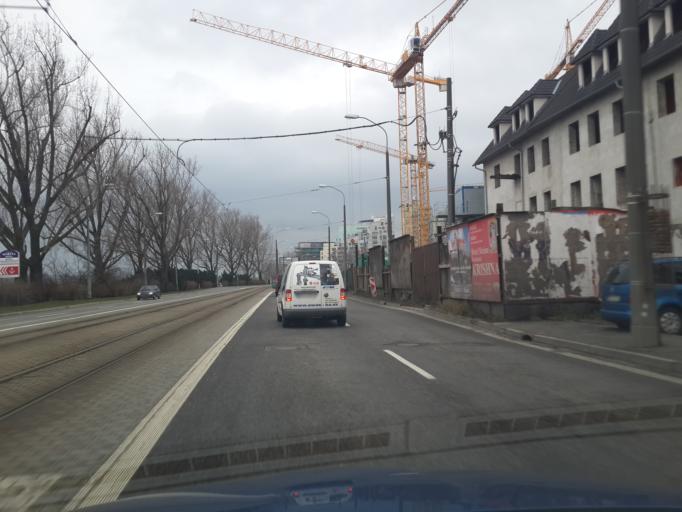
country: SK
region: Bratislavsky
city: Bratislava
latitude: 48.1401
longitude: 17.0976
